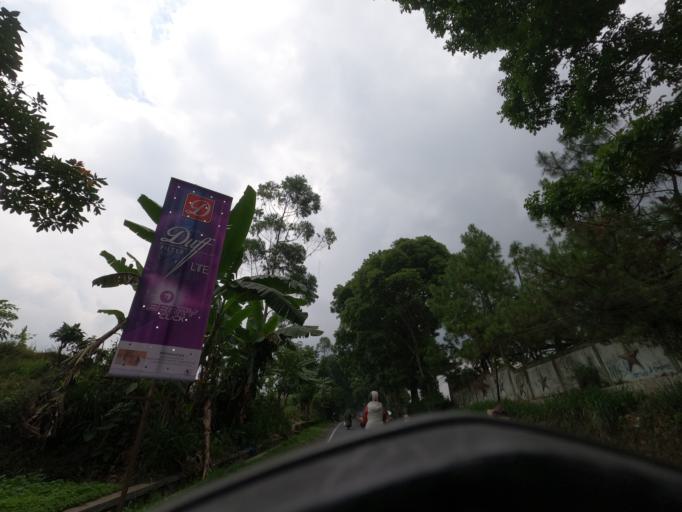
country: ID
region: West Java
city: Sukabumi
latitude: -6.7684
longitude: 107.0581
